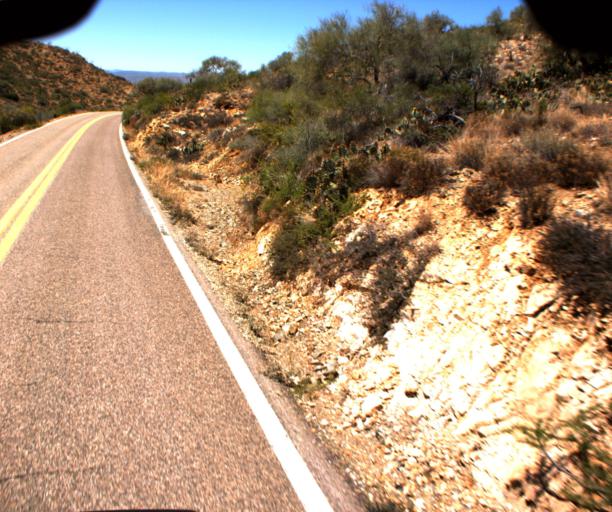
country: US
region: Arizona
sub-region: Yavapai County
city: Bagdad
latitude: 34.4475
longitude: -112.9709
